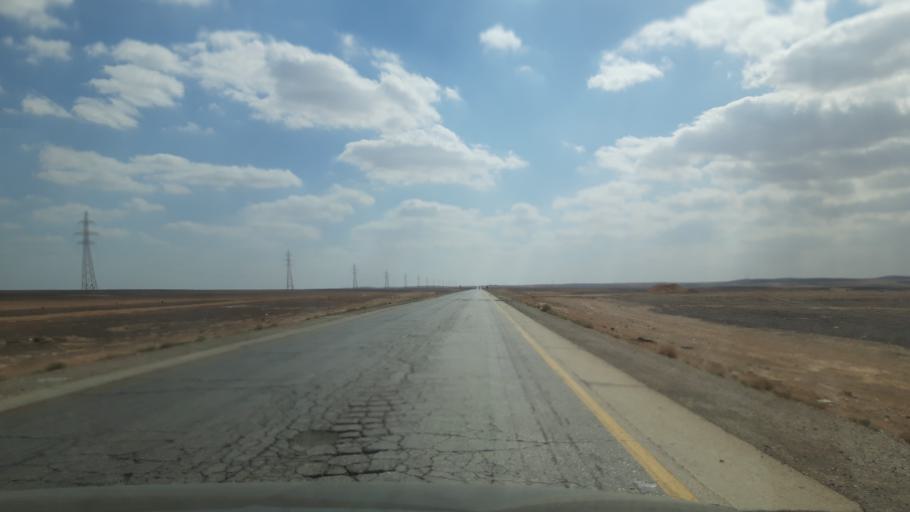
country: JO
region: Amman
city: Al Azraq ash Shamali
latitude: 31.7749
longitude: 36.5676
